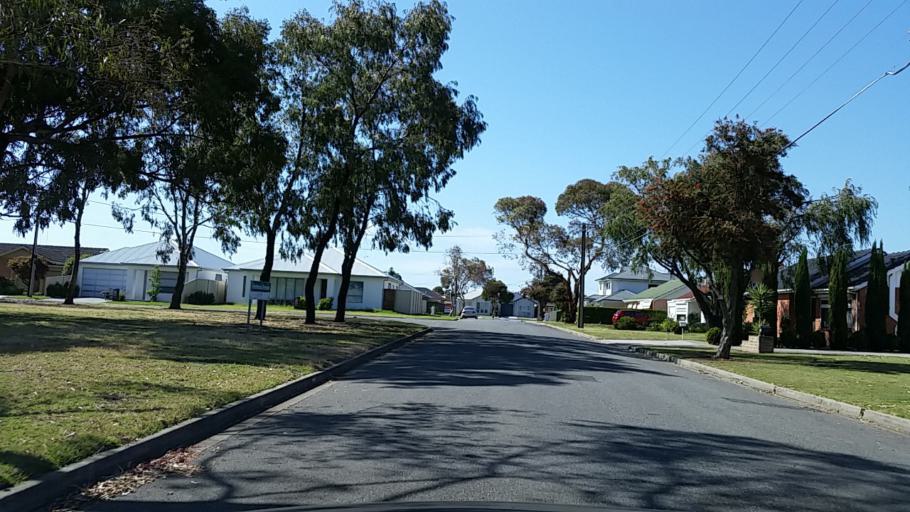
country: AU
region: South Australia
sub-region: Charles Sturt
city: Grange
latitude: -34.9109
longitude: 138.5034
